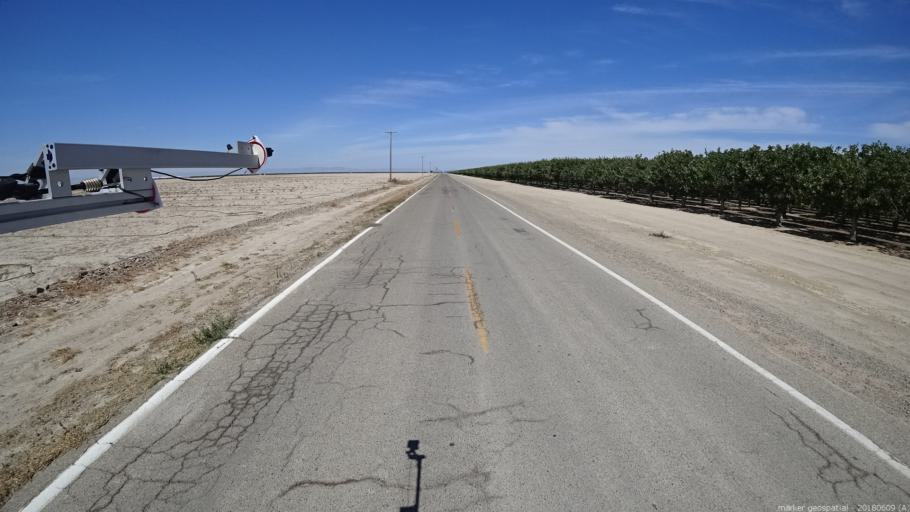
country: US
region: California
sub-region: Fresno County
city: Firebaugh
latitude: 36.9525
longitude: -120.3649
